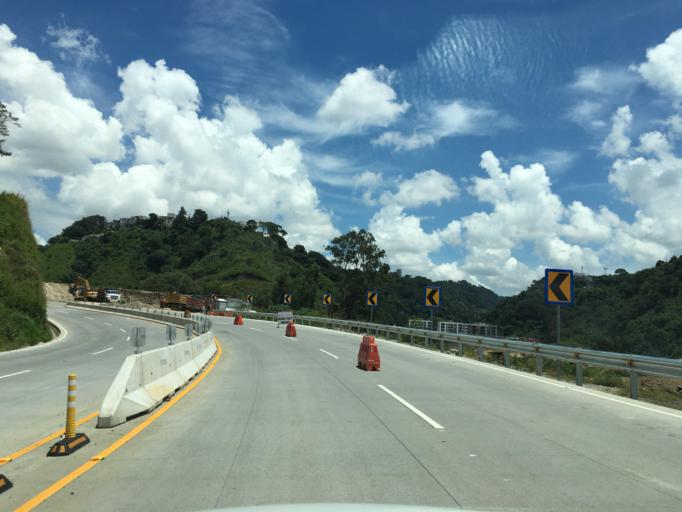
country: GT
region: Guatemala
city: Santa Catarina Pinula
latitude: 14.5495
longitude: -90.5317
